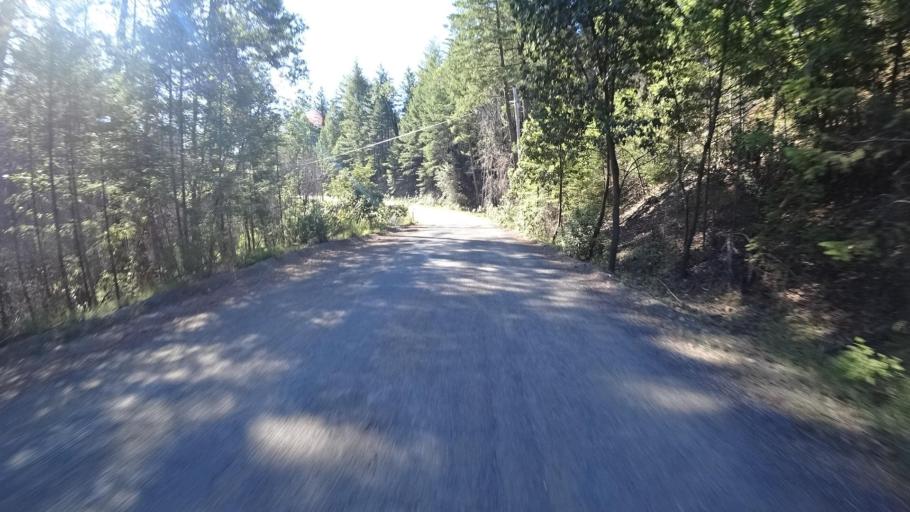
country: US
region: California
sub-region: Lake County
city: Upper Lake
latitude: 39.4029
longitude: -122.9629
